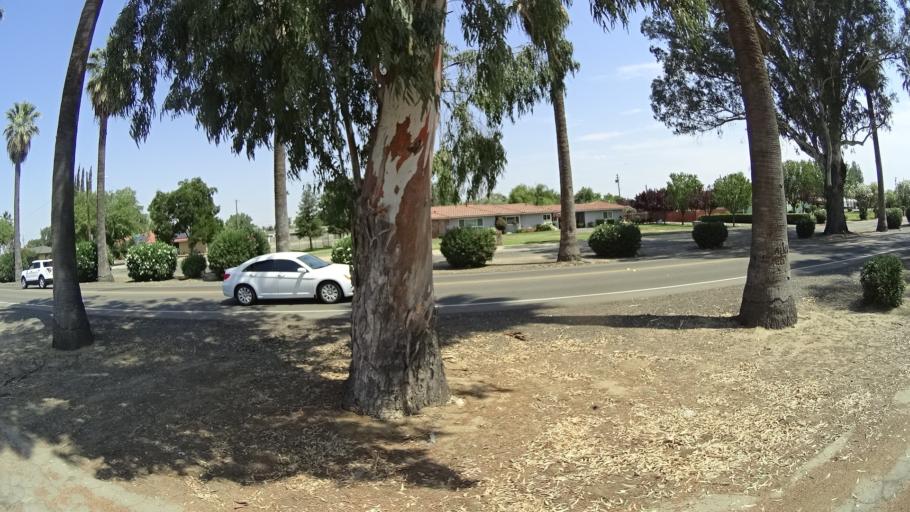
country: US
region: California
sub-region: Fresno County
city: West Park
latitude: 36.7281
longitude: -119.8321
